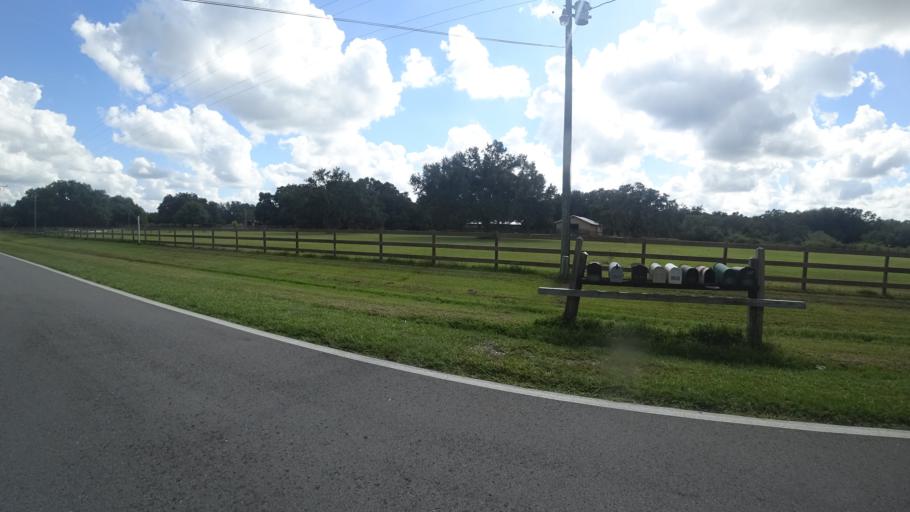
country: US
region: Florida
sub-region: Sarasota County
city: Lake Sarasota
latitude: 27.2889
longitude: -82.2282
